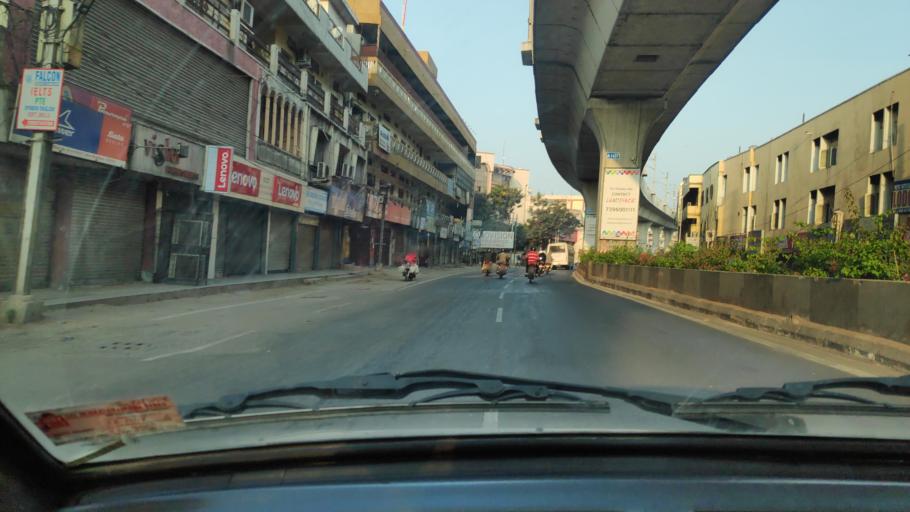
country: IN
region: Telangana
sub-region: Rangareddi
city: Gaddi Annaram
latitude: 17.3736
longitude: 78.5013
